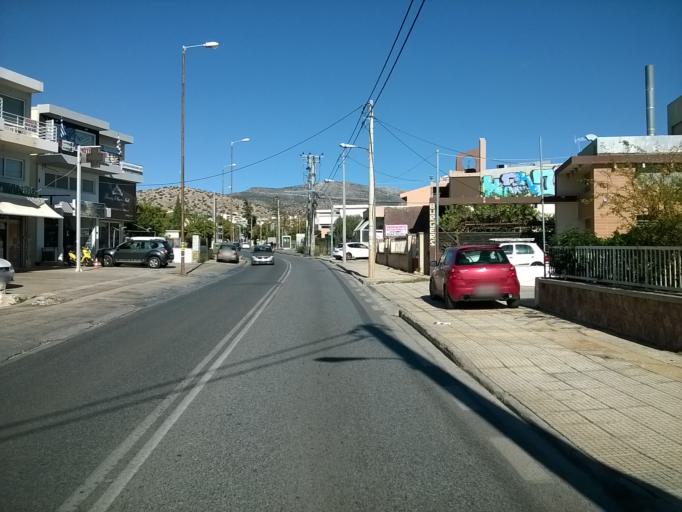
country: GR
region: Attica
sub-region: Nomarchia Anatolikis Attikis
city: Vari
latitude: 37.8270
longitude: 23.8039
